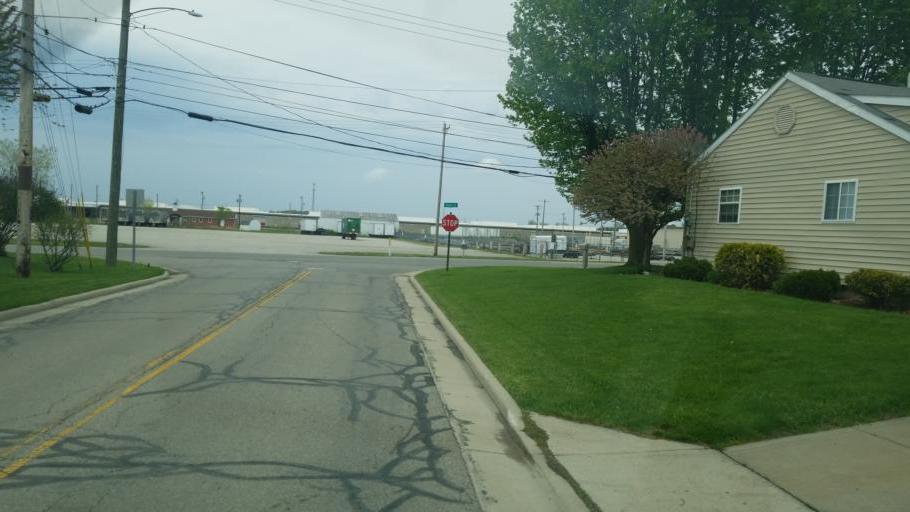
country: US
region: Ohio
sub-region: Richland County
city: Shelby
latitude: 40.8955
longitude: -82.6660
